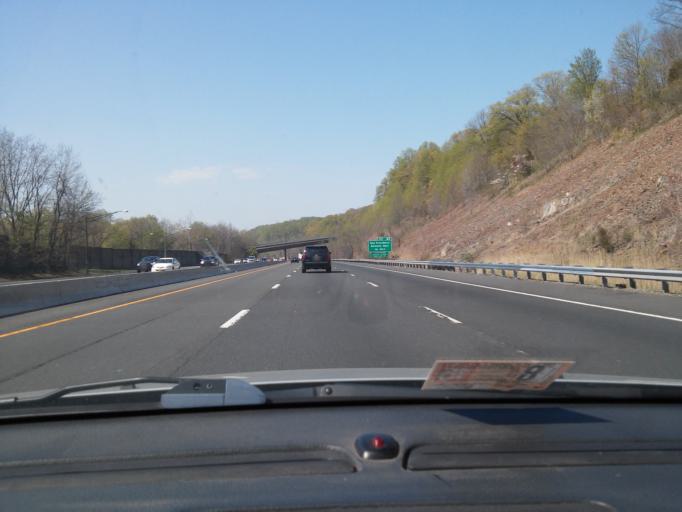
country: US
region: New Jersey
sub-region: Union County
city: New Providence
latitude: 40.6805
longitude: -74.3957
